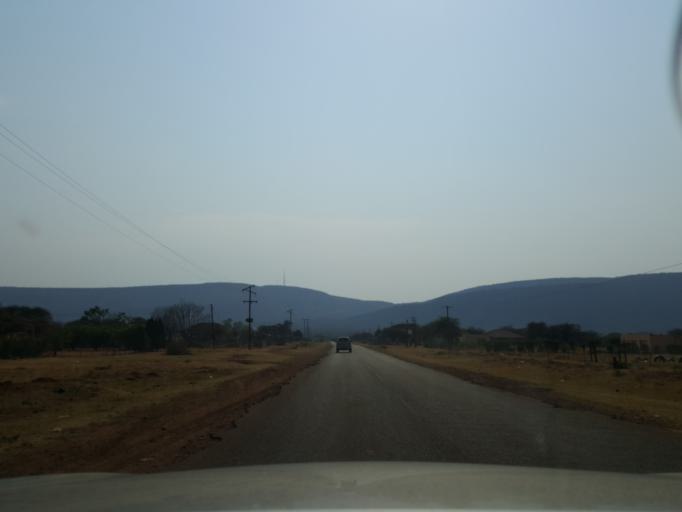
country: BW
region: South East
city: Lobatse
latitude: -25.2969
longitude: 25.8412
